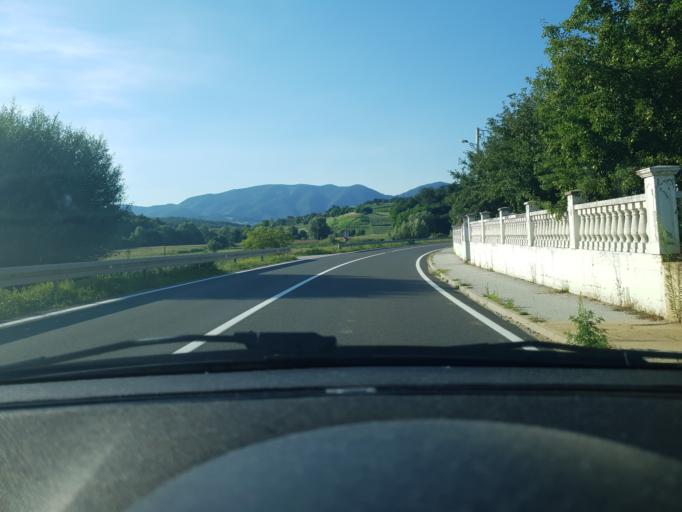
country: HR
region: Krapinsko-Zagorska
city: Mihovljan
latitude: 46.1346
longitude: 15.9375
